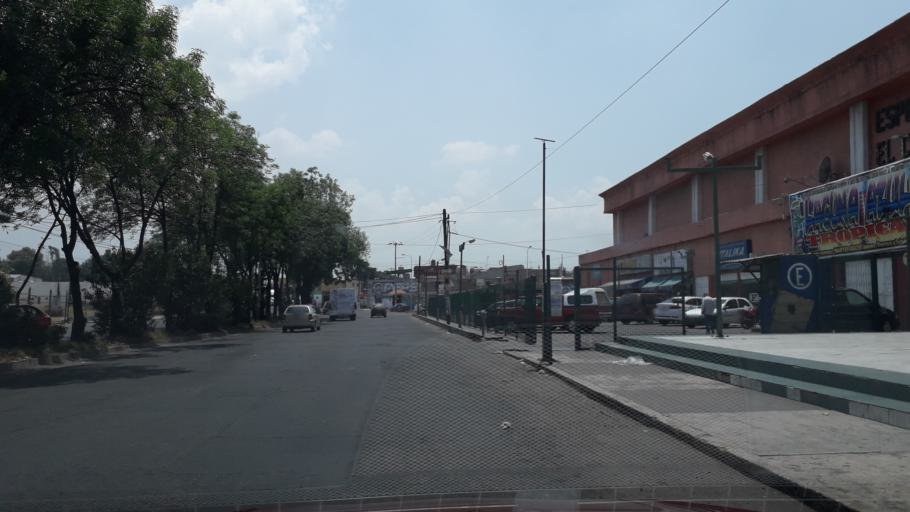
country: MX
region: Puebla
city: Puebla
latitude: 19.0494
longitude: -98.1664
